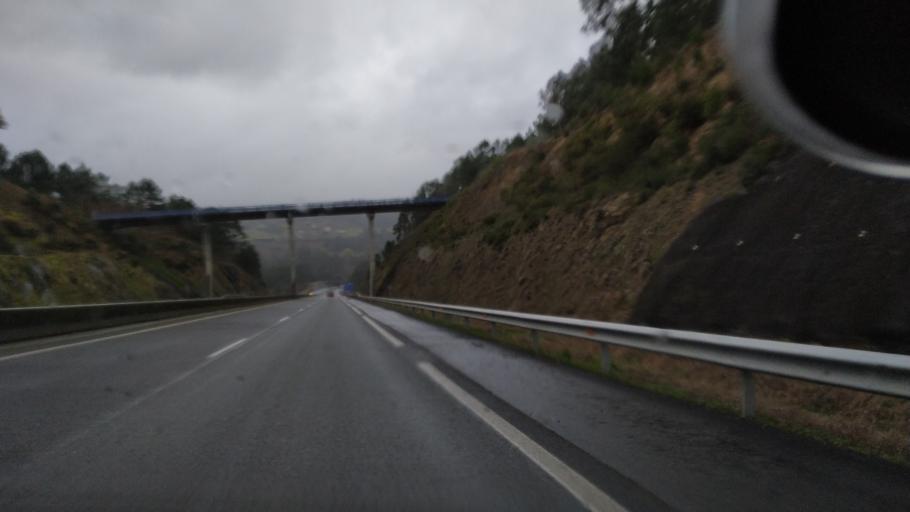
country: ES
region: Galicia
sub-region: Provincia da Coruna
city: Vedra
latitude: 42.8251
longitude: -8.5121
